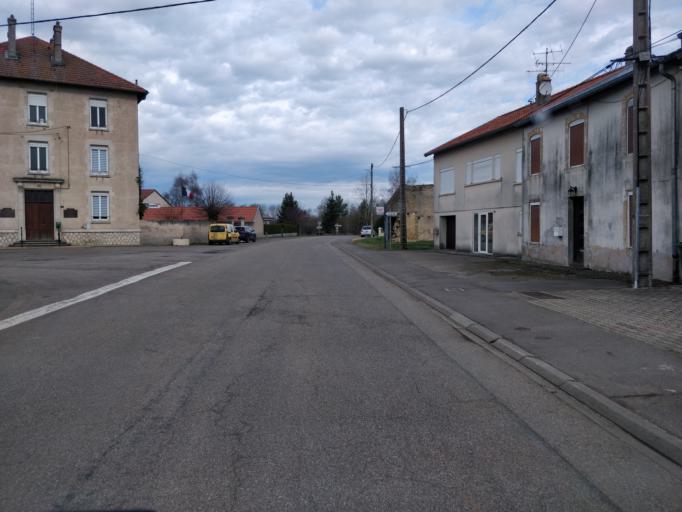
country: FR
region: Lorraine
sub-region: Departement de Meurthe-et-Moselle
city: Jarny
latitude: 49.1003
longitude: 5.8900
